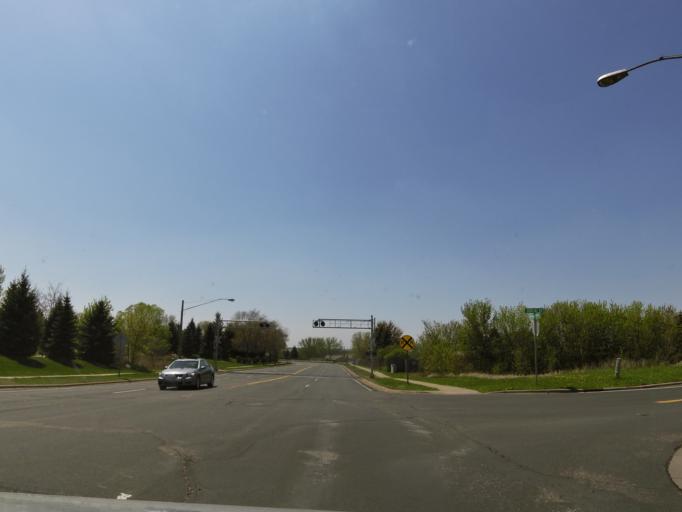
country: US
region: Minnesota
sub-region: Scott County
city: Savage
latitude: 44.7532
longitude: -93.3164
